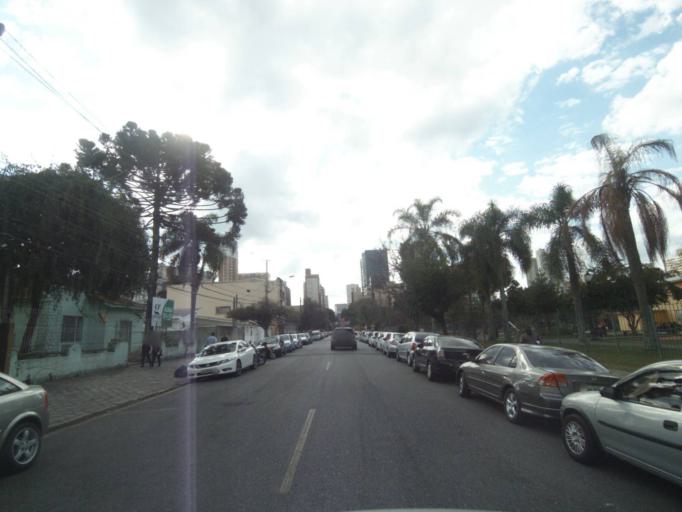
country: BR
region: Parana
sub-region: Curitiba
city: Curitiba
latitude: -25.4446
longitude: -49.2721
